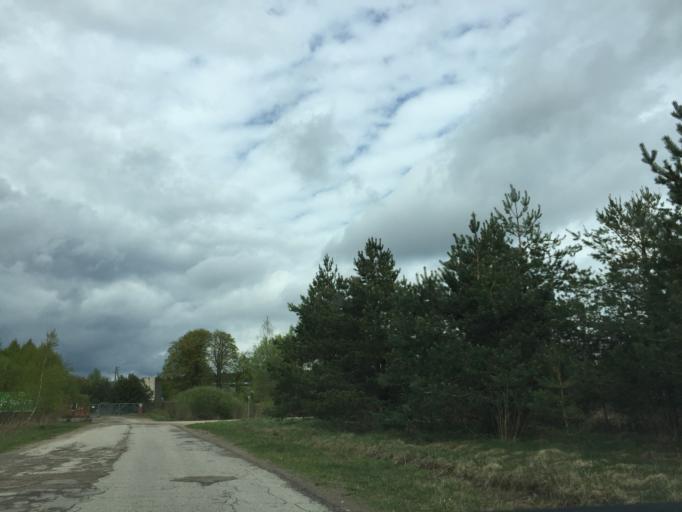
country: LV
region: Kekava
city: Kekava
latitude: 56.7898
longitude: 24.3017
